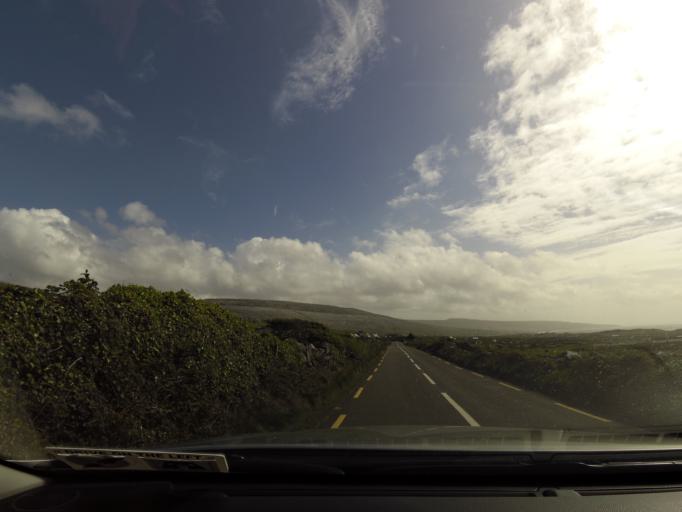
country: IE
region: Connaught
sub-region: County Galway
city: Bearna
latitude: 53.1359
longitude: -9.2751
